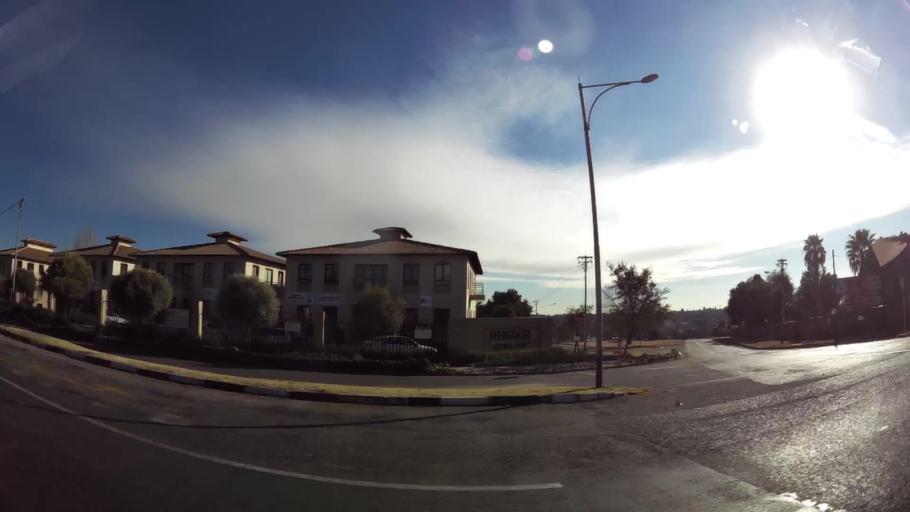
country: ZA
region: Gauteng
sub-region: City of Johannesburg Metropolitan Municipality
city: Roodepoort
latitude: -26.1275
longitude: 27.8351
